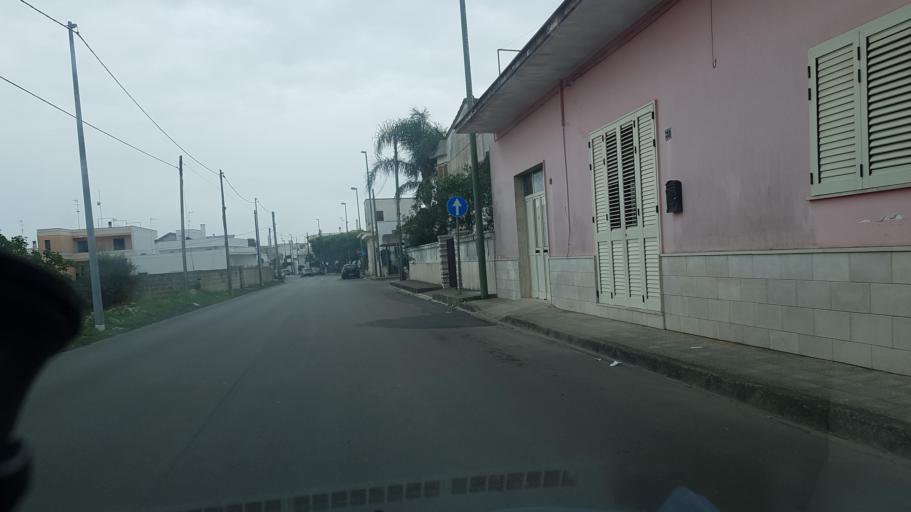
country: IT
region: Apulia
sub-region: Provincia di Lecce
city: Veglie
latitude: 40.3379
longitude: 17.9568
